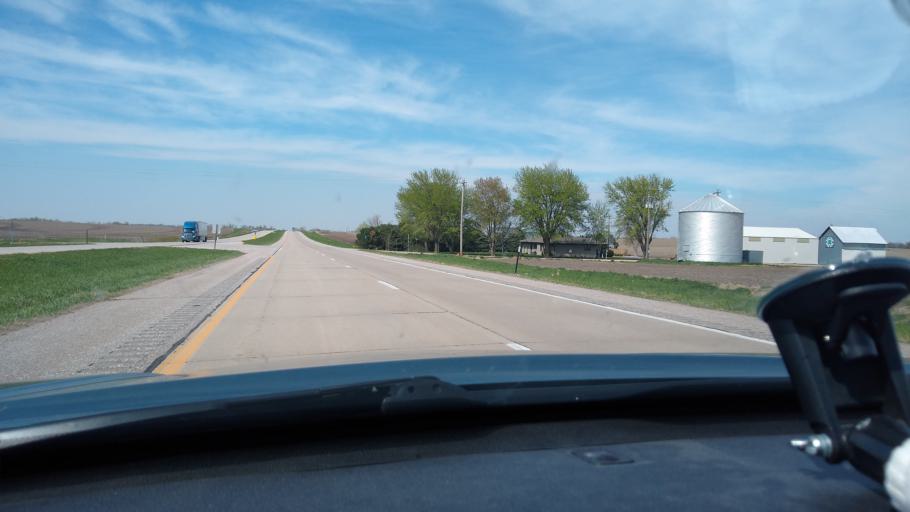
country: US
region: Nebraska
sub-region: Fillmore County
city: Geneva
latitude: 40.3642
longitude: -97.5774
